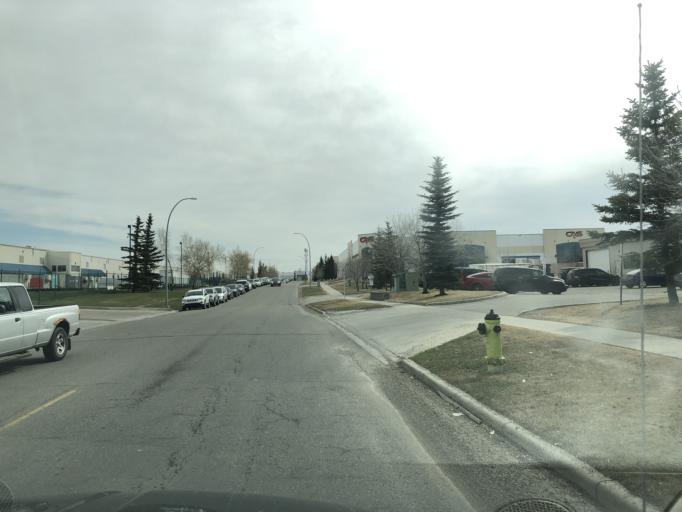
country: CA
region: Alberta
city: Calgary
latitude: 51.0718
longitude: -113.9980
